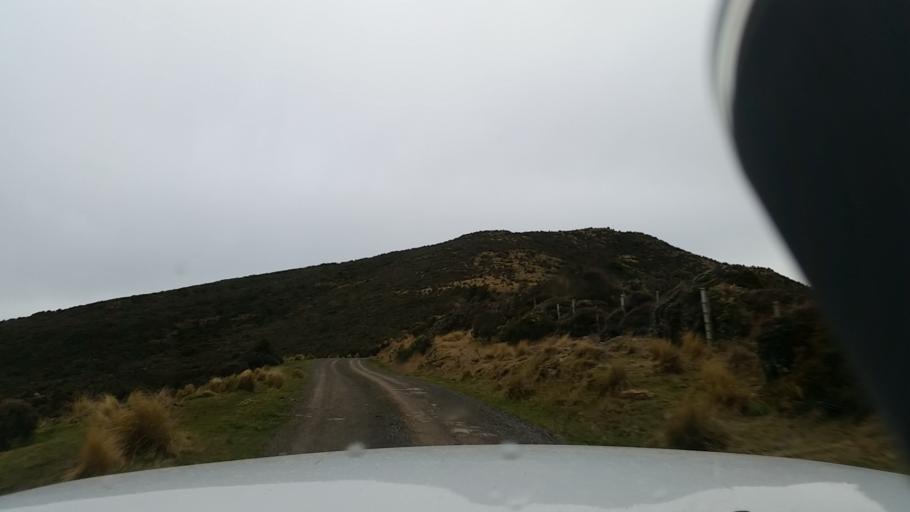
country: NZ
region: Canterbury
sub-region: Christchurch City
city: Christchurch
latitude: -43.8457
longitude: 172.8819
